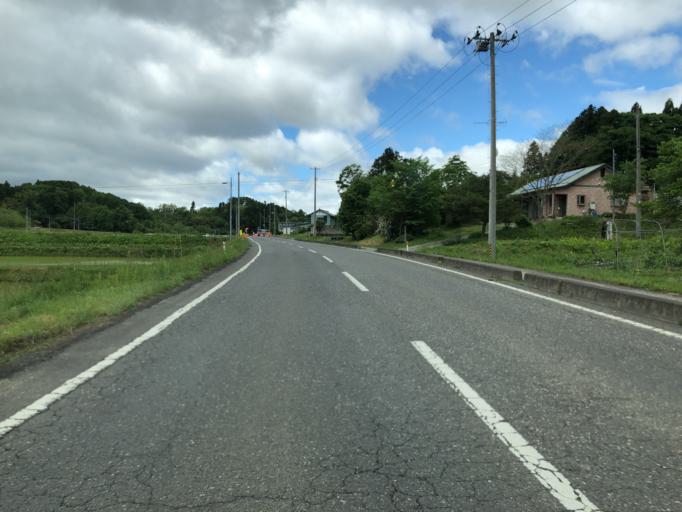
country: JP
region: Fukushima
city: Motomiya
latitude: 37.4975
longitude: 140.4644
